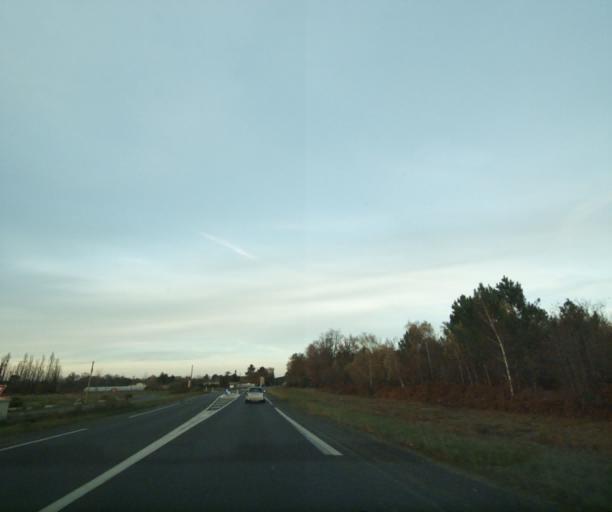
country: FR
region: Aquitaine
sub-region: Departement de la Gironde
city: Bazas
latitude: 44.4518
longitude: -0.2337
